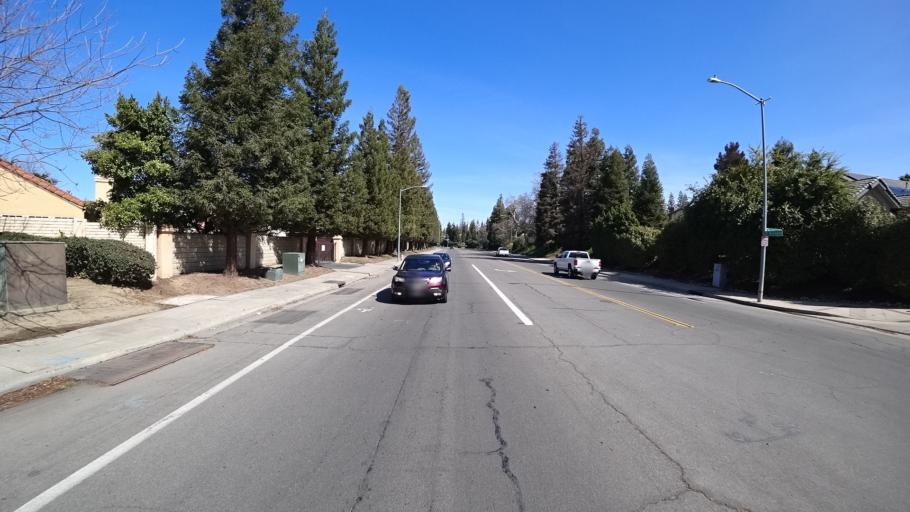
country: US
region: California
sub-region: Fresno County
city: Clovis
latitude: 36.8754
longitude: -119.7724
